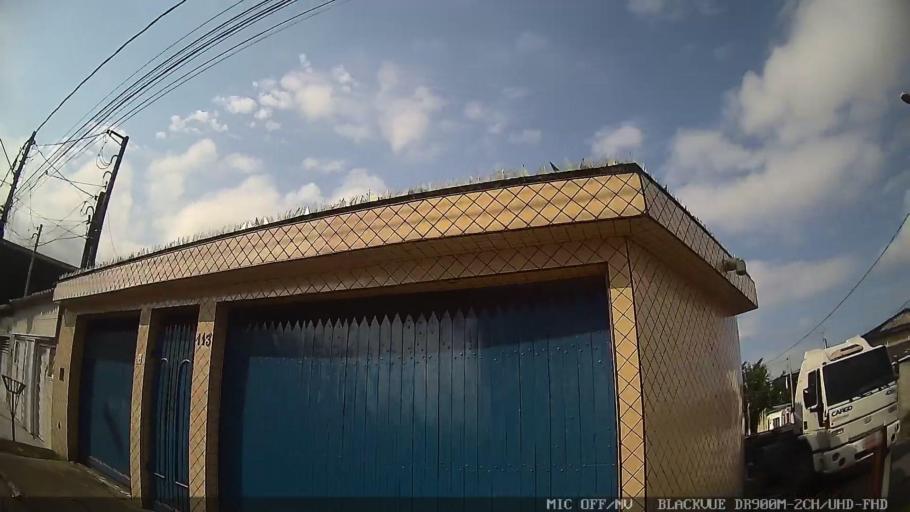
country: BR
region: Sao Paulo
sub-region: Santos
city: Santos
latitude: -23.9491
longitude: -46.2856
